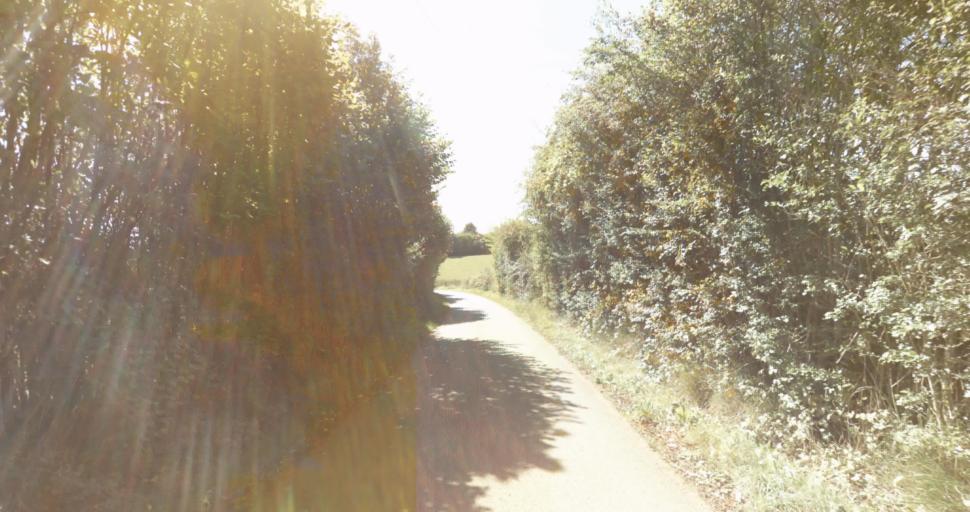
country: FR
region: Lower Normandy
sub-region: Departement de l'Orne
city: Gace
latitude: 48.7711
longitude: 0.2860
